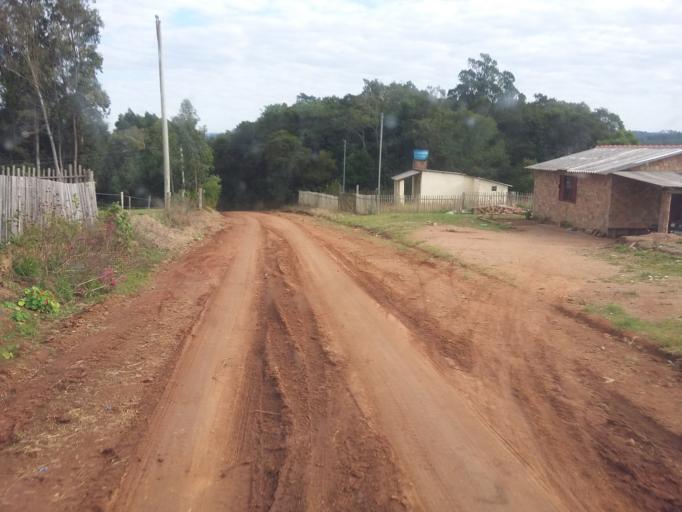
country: BR
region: Rio Grande do Sul
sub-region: Camaqua
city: Camaqua
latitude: -30.7113
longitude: -51.7711
